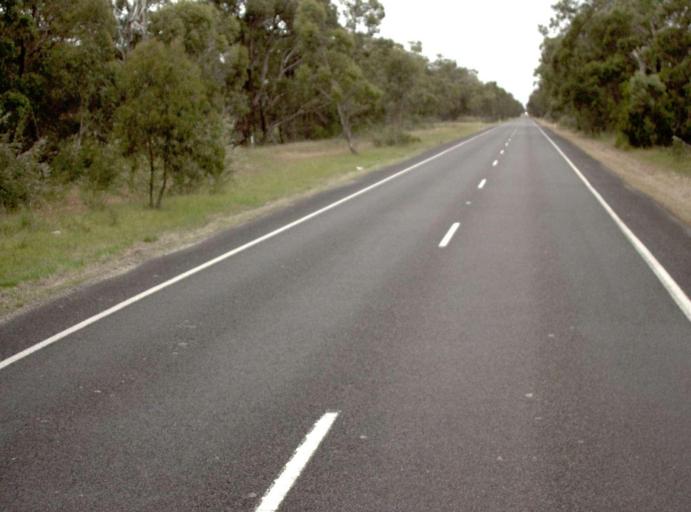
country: AU
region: Victoria
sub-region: Wellington
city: Sale
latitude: -38.3524
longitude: 146.9973
